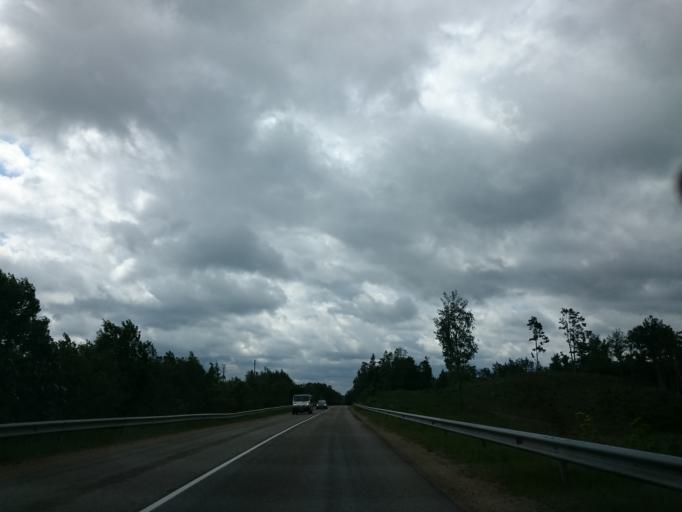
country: LV
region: Madonas Rajons
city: Madona
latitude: 56.8745
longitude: 26.1791
